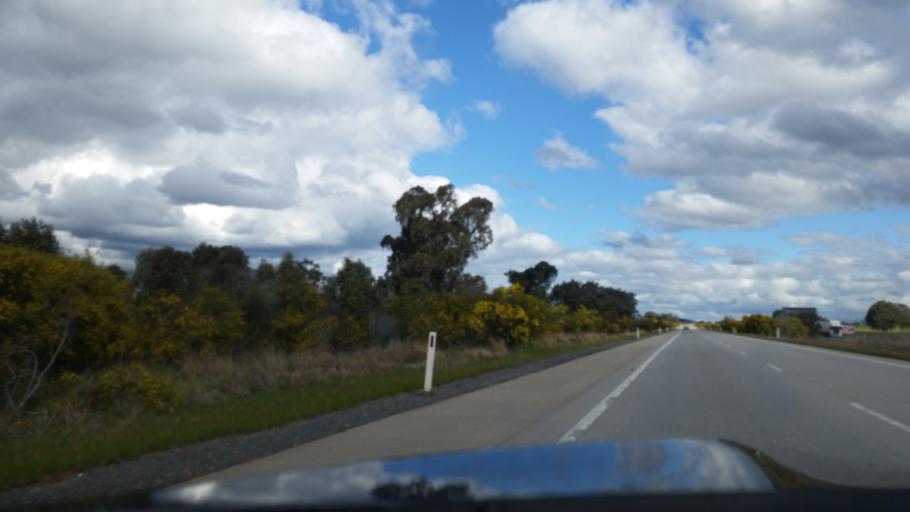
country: AU
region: New South Wales
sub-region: Greater Hume Shire
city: Jindera
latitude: -35.9429
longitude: 147.0037
